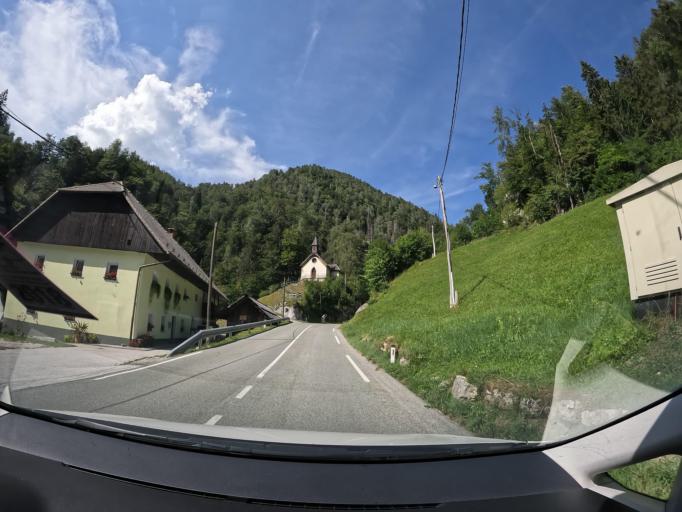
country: SI
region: Trzic
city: Trzic
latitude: 46.4116
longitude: 14.2998
